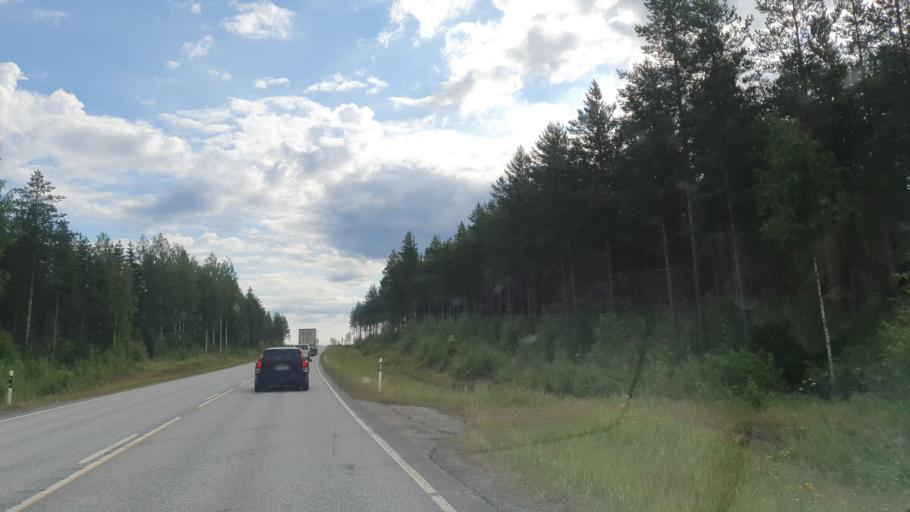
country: FI
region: Central Finland
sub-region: Jyvaeskylae
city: Hankasalmi
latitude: 62.3907
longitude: 26.6210
